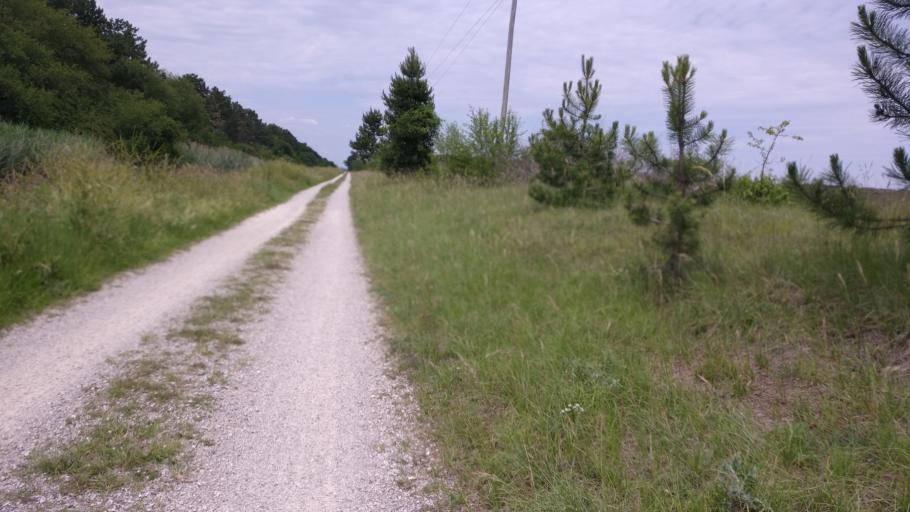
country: AT
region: Lower Austria
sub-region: Politischer Bezirk Wiener Neustadt
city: Lichtenworth
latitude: 47.8649
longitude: 16.2816
